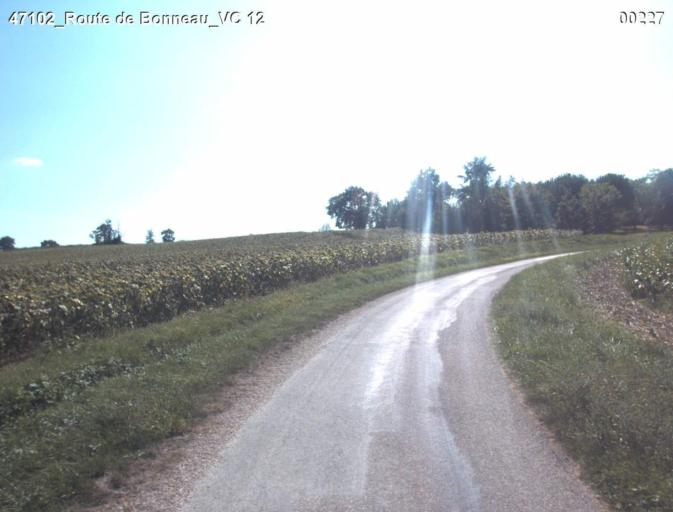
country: FR
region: Aquitaine
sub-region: Departement du Lot-et-Garonne
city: Nerac
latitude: 44.0848
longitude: 0.4131
